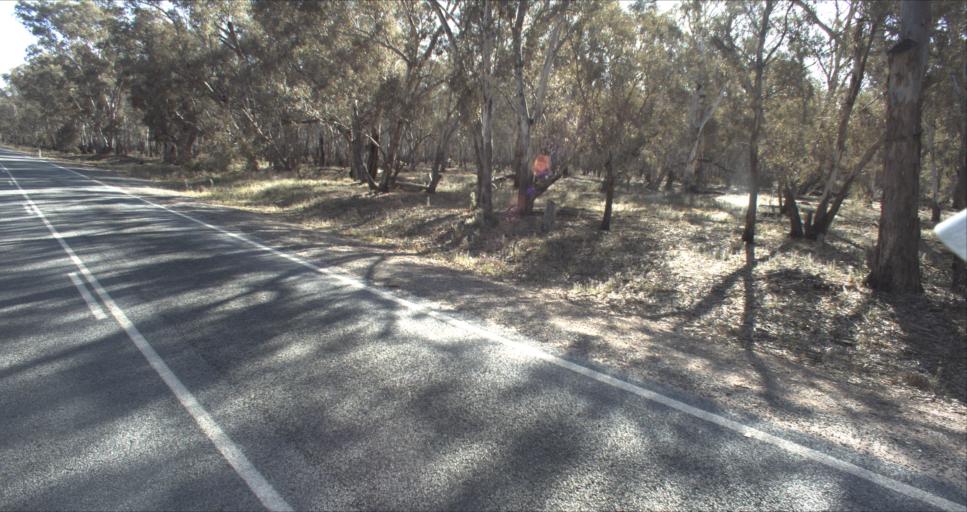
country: AU
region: New South Wales
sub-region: Leeton
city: Leeton
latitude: -34.6257
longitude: 146.3796
